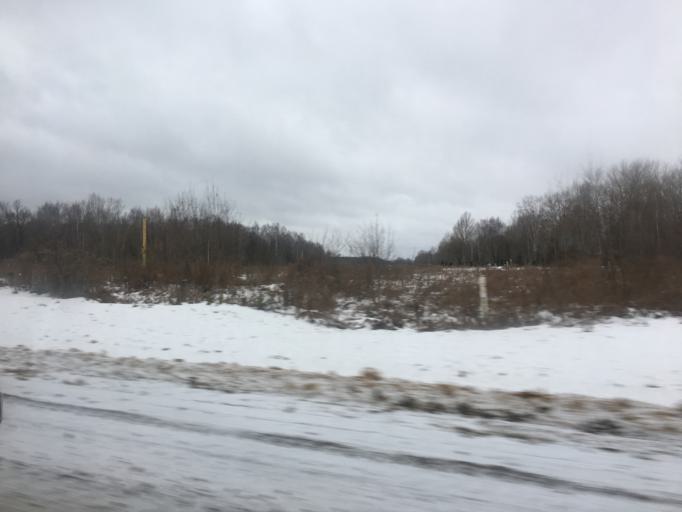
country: RU
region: Tula
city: Pervomayskiy
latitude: 54.0571
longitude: 37.5318
